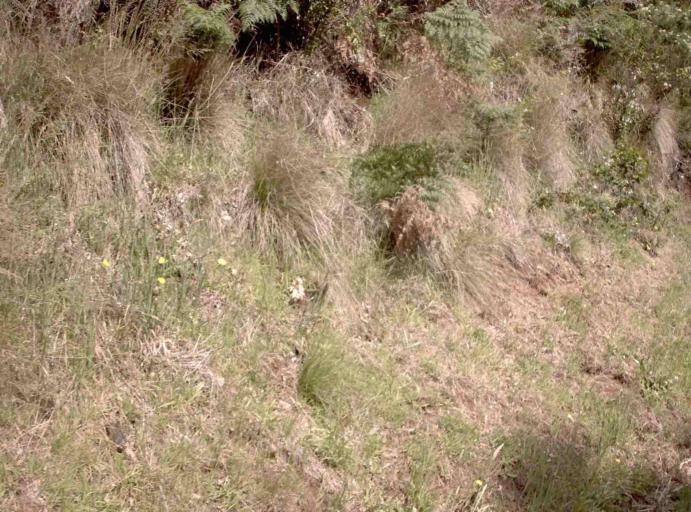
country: AU
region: Victoria
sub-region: Latrobe
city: Traralgon
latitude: -38.3475
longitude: 146.5684
